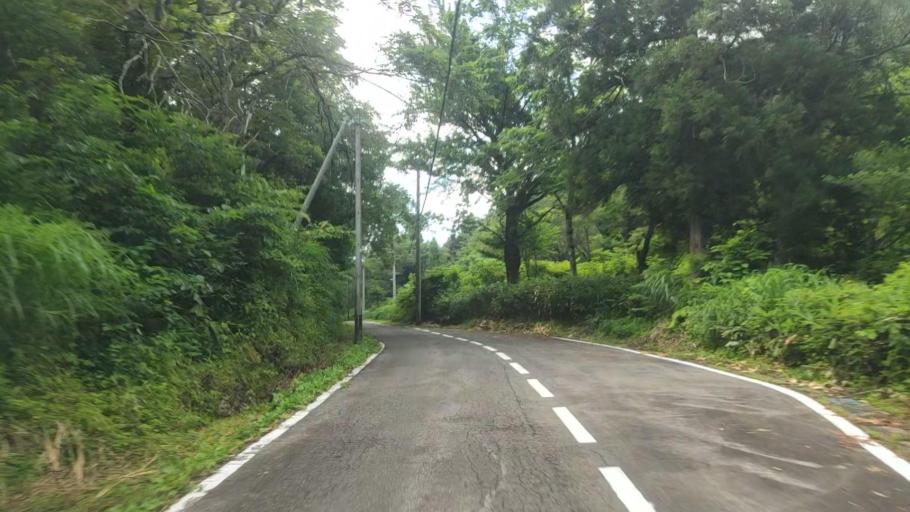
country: JP
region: Fukui
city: Katsuyama
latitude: 36.2033
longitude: 136.5251
